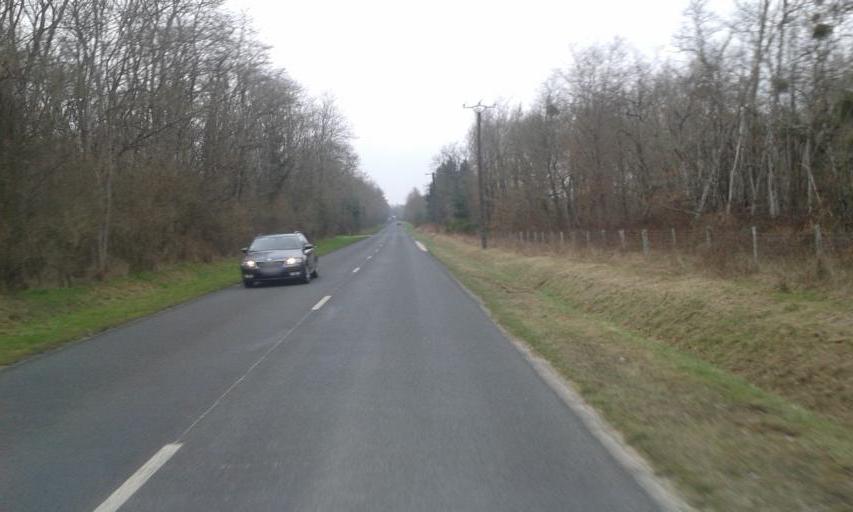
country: FR
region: Centre
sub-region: Departement du Loiret
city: Lailly-en-Val
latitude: 47.7225
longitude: 1.6570
